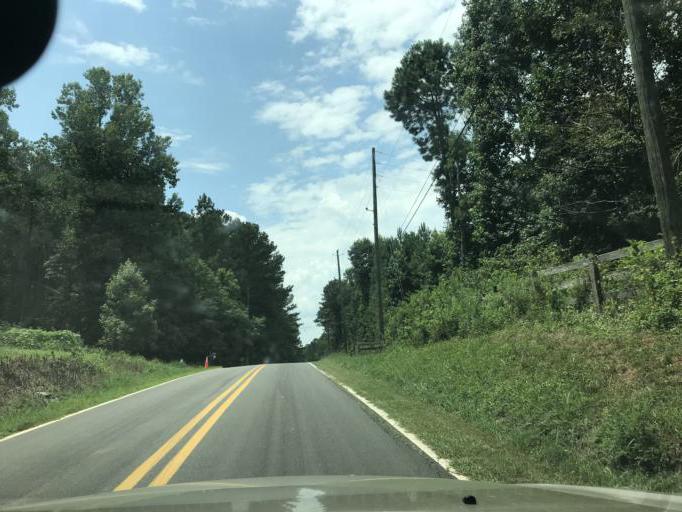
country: US
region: Georgia
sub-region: Dawson County
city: Dawsonville
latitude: 34.3301
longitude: -84.2093
